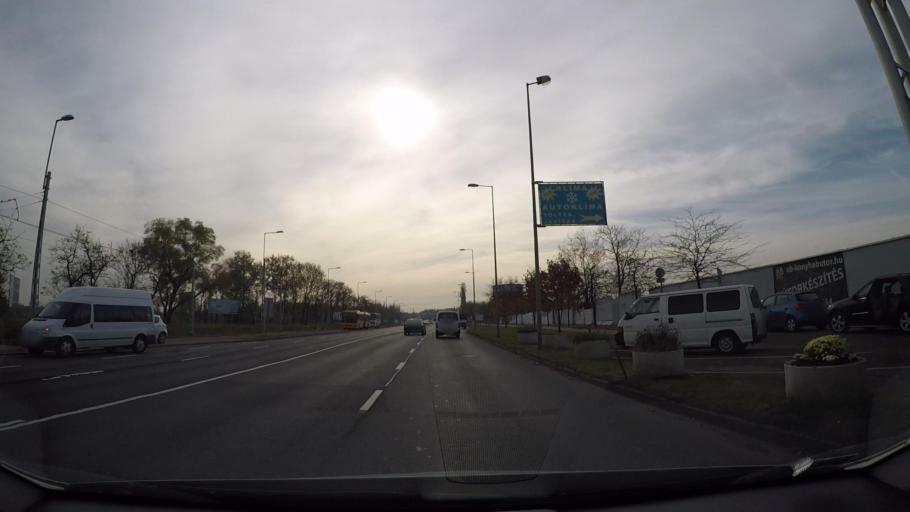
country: HU
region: Budapest
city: Budapest X. keruelet
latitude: 47.4994
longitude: 19.1373
